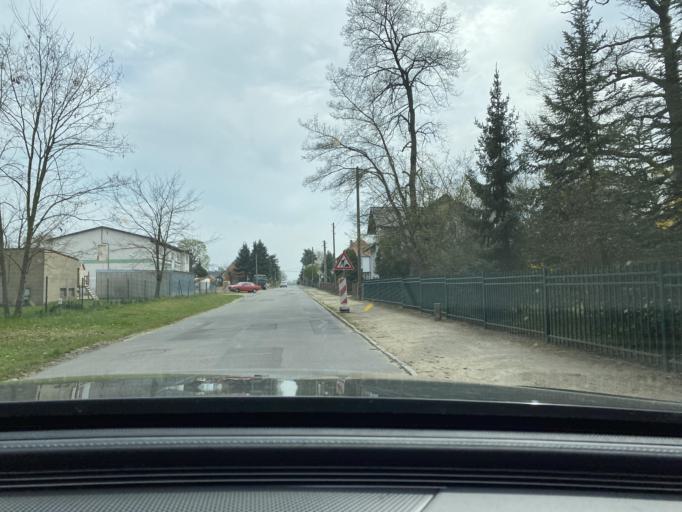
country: DE
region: Saxony
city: Neschwitz
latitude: 51.2673
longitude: 14.3296
